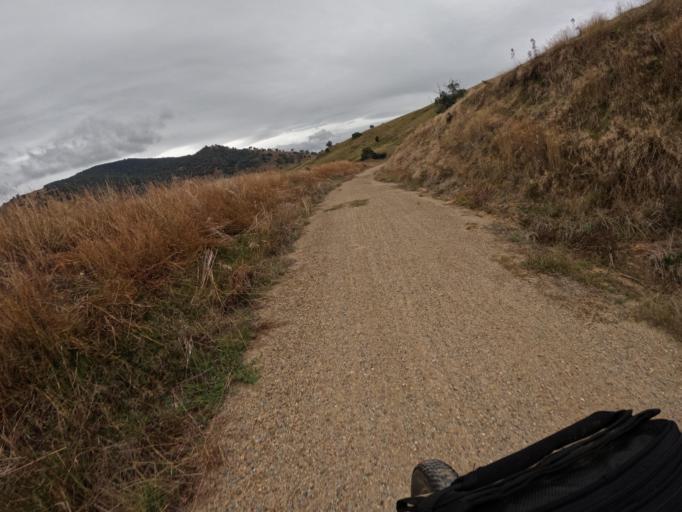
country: AU
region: New South Wales
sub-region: Albury Municipality
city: East Albury
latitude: -36.1832
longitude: 147.3719
